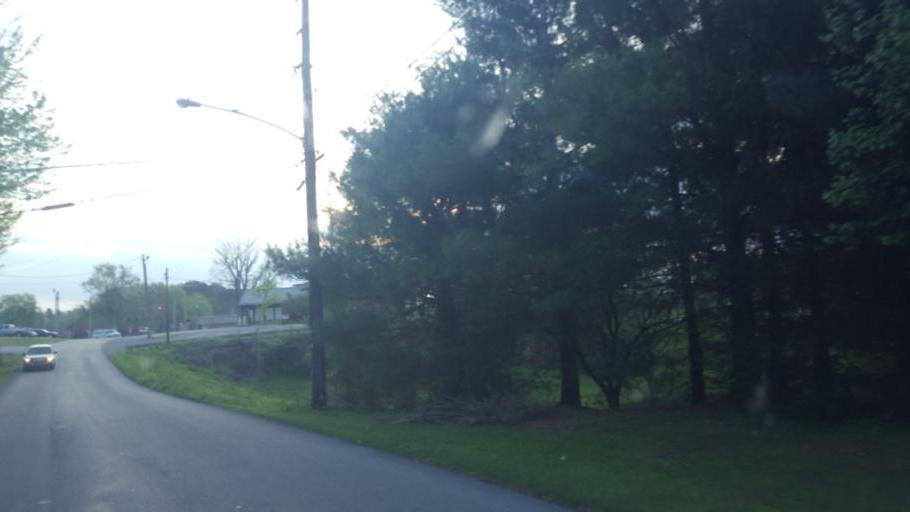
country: US
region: Kentucky
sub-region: Hart County
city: Munfordville
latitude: 37.2789
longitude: -85.8997
